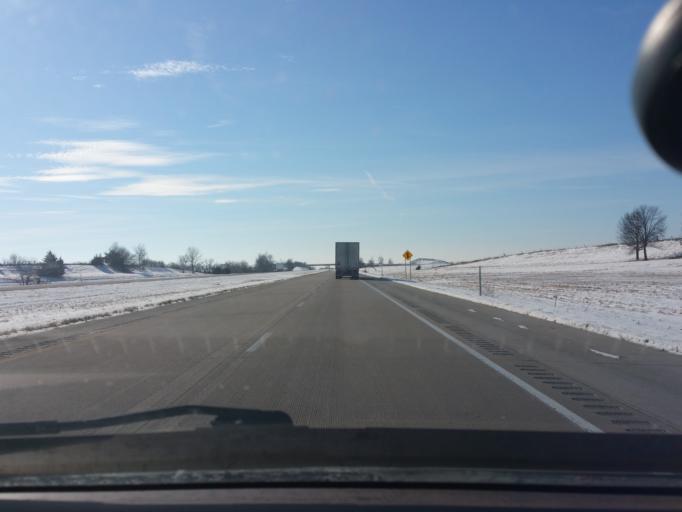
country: US
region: Iowa
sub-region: Decatur County
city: Leon
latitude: 40.8111
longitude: -93.8278
